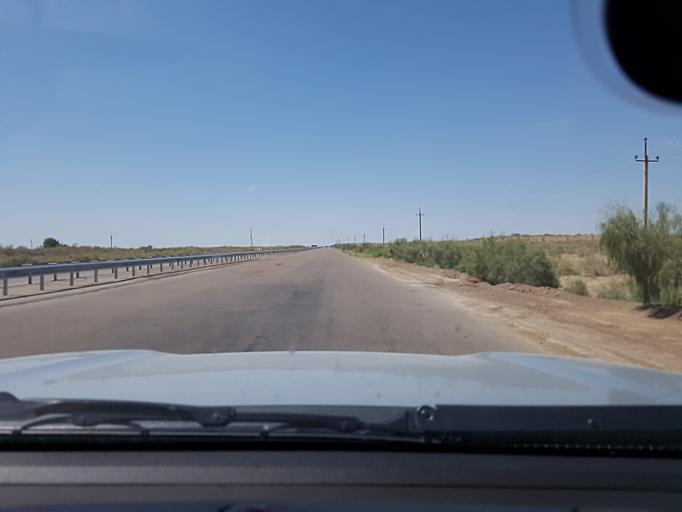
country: TM
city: Akdepe
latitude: 41.7516
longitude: 59.2903
